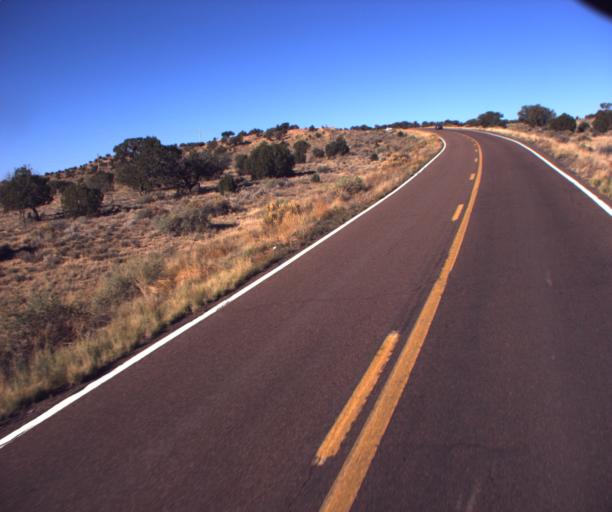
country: US
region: Arizona
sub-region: Apache County
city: Ganado
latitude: 35.7545
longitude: -109.8954
